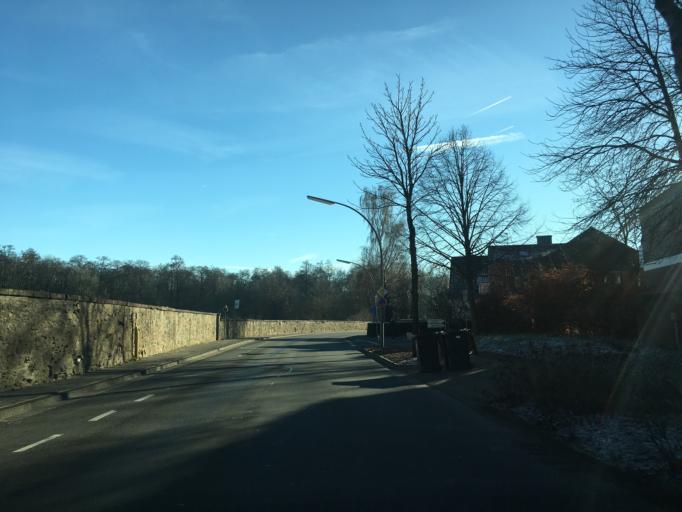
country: DE
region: North Rhine-Westphalia
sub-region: Regierungsbezirk Munster
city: Steinfurt
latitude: 52.1424
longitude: 7.3410
